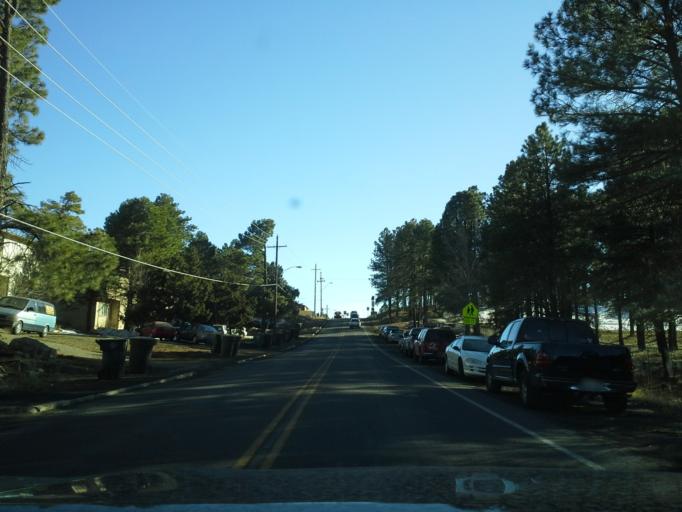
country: US
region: Arizona
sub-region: Coconino County
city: Flagstaff
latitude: 35.1830
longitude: -111.6483
